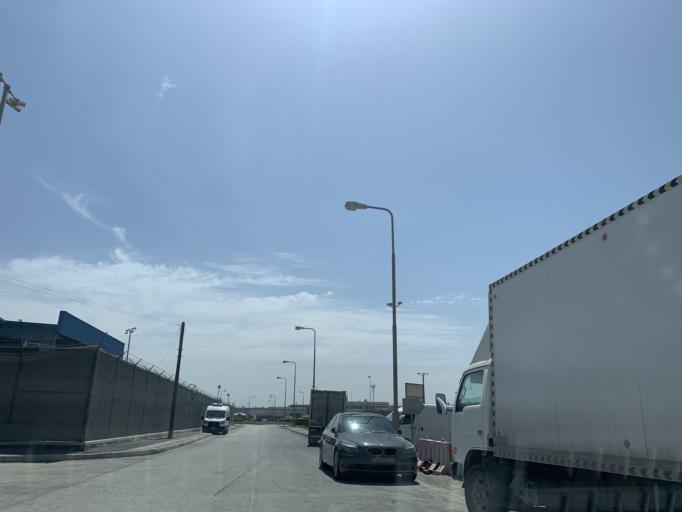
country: BH
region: Muharraq
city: Al Muharraq
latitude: 26.2727
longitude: 50.6190
